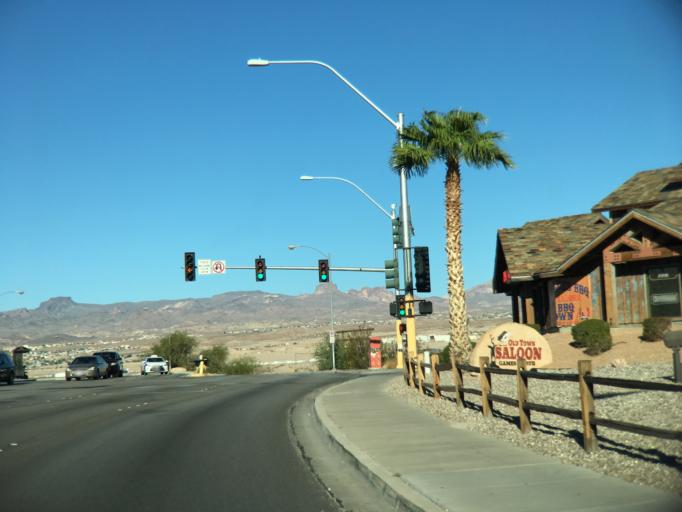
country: US
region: Arizona
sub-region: Mohave County
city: Bullhead City
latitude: 35.1459
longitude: -114.5791
